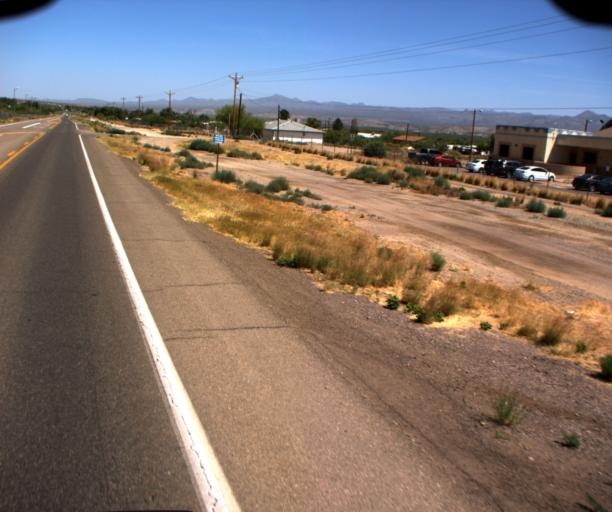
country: US
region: Arizona
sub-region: Graham County
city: Bylas
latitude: 33.1253
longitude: -110.1147
